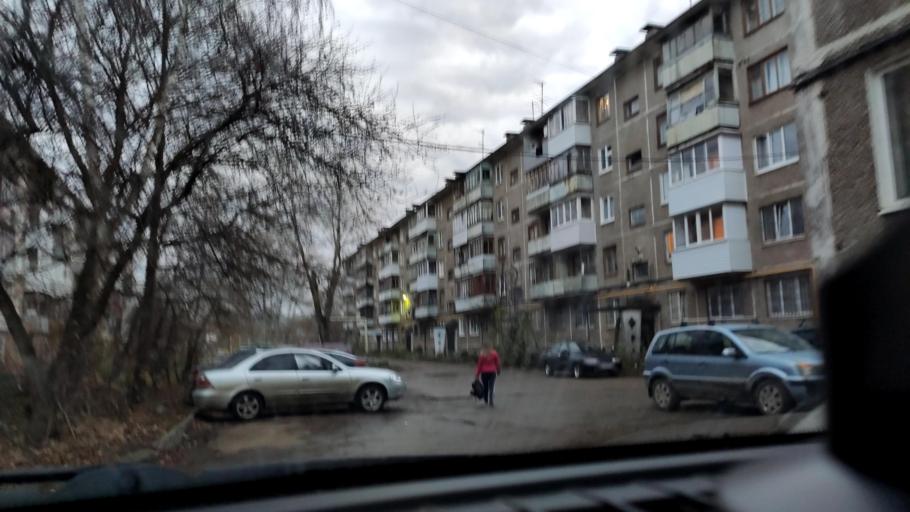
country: RU
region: Perm
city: Perm
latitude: 57.9775
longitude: 56.2786
